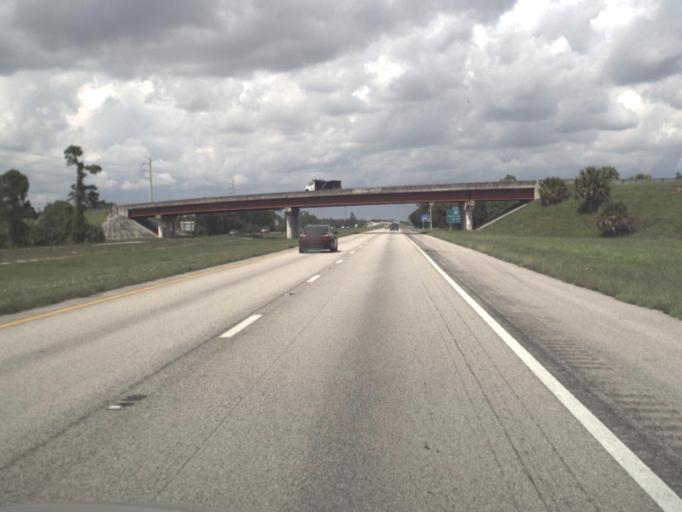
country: US
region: Florida
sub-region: Charlotte County
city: Punta Gorda
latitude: 26.9252
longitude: -82.0144
